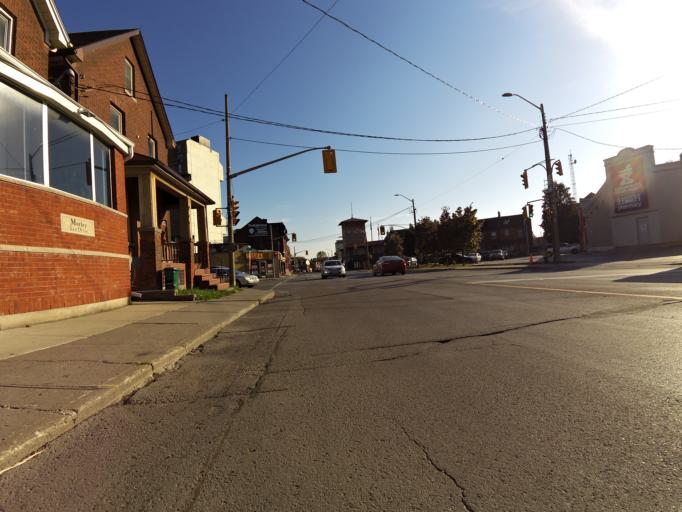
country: CA
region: Ontario
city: Kingston
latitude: 44.2344
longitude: -76.4932
